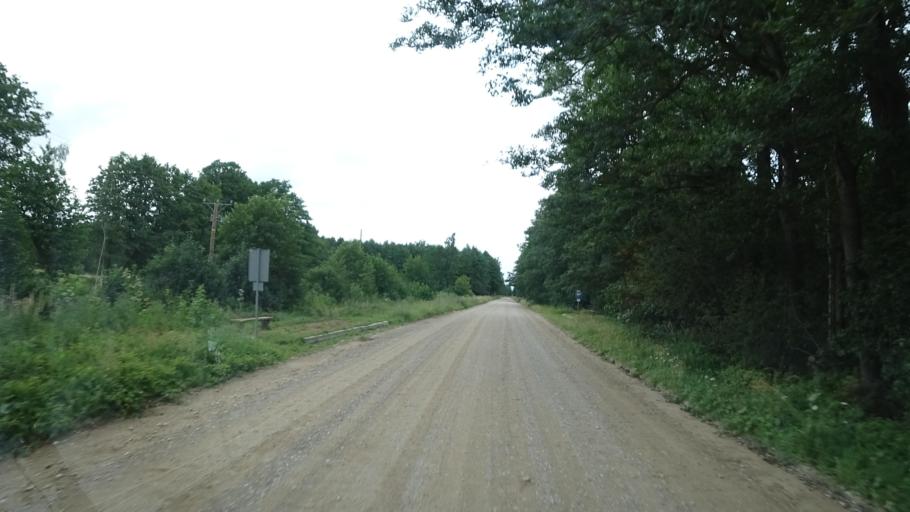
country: LV
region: Liepaja
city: Vec-Liepaja
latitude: 56.6212
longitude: 21.0424
